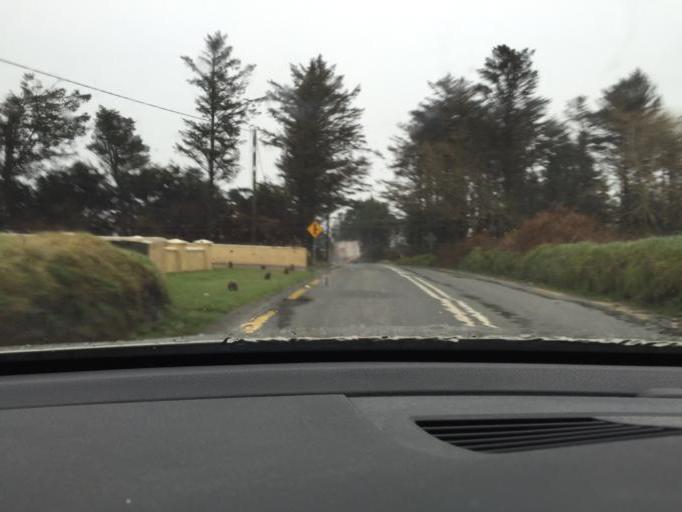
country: IE
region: Munster
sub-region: Ciarrai
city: Dingle
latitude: 52.1451
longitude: -10.1353
